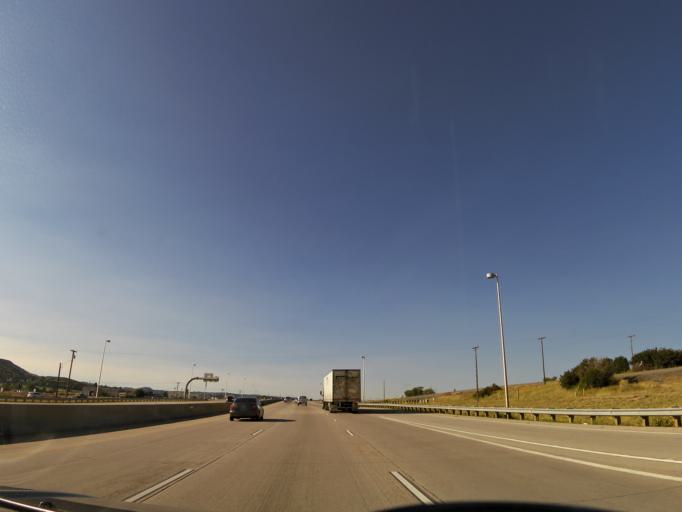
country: US
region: Colorado
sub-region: Douglas County
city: Castle Rock
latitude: 39.3629
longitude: -104.8668
